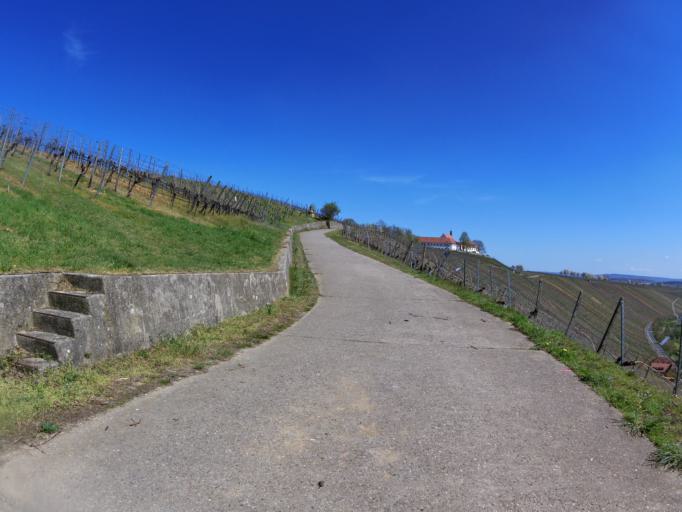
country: DE
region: Bavaria
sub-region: Regierungsbezirk Unterfranken
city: Nordheim
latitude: 49.8655
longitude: 10.1778
